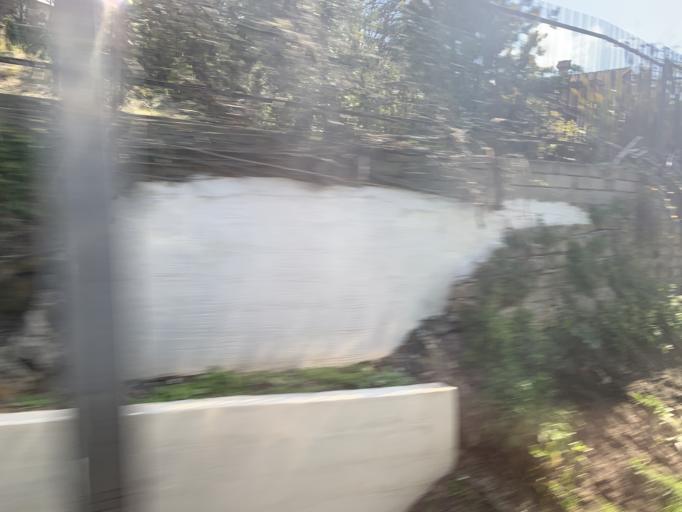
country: IT
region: Latium
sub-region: Citta metropolitana di Roma Capitale
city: Marino
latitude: 41.7714
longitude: 12.6468
